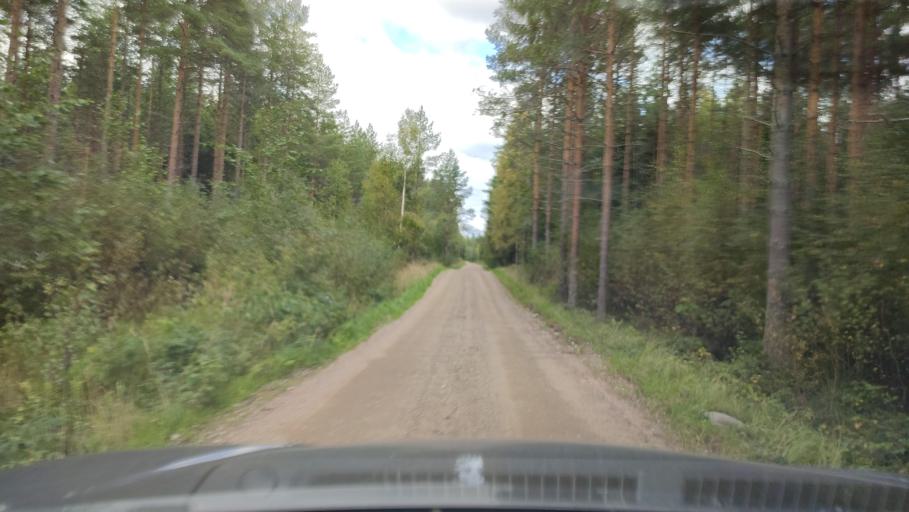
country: FI
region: Southern Ostrobothnia
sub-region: Suupohja
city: Karijoki
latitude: 62.2045
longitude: 21.6152
